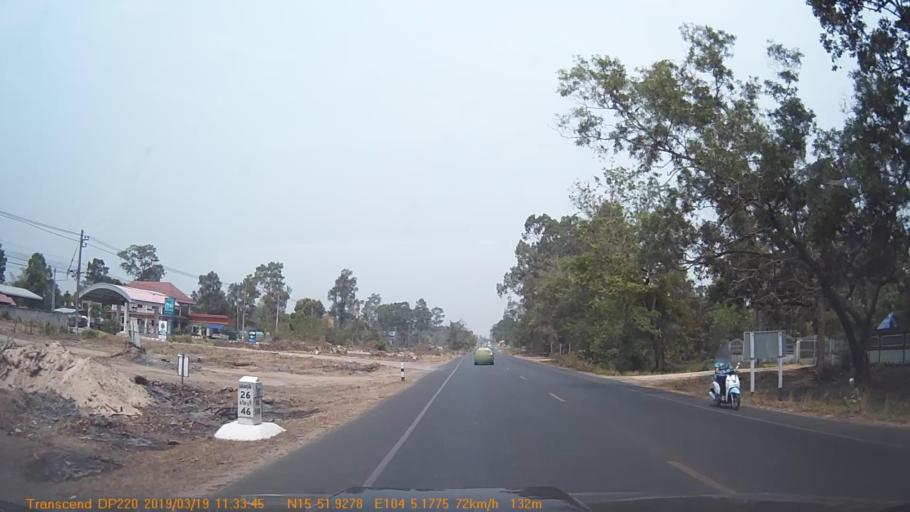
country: TH
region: Yasothon
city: Yasothon
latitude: 15.8657
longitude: 104.0861
